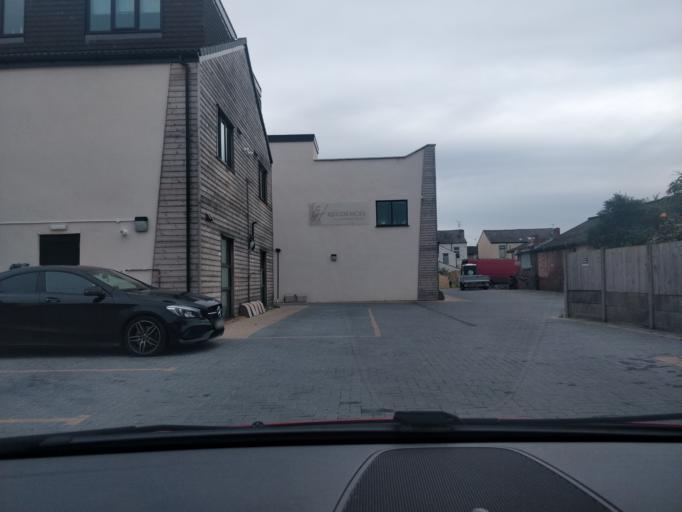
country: GB
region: England
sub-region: Sefton
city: Southport
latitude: 53.6463
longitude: -2.9931
